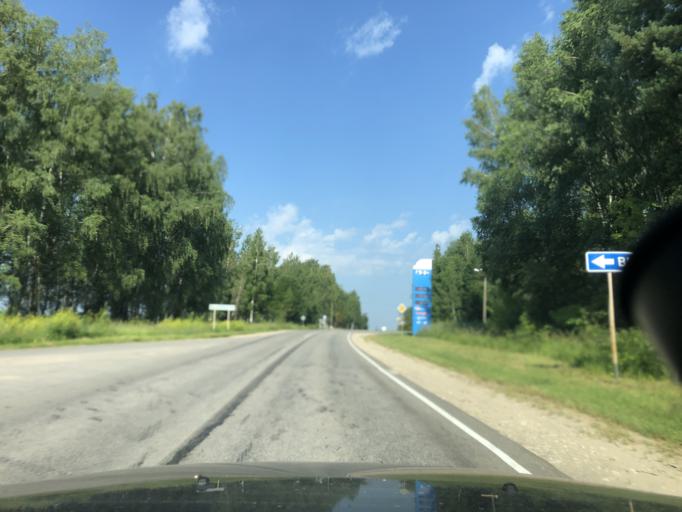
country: RU
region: Tula
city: Dubna
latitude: 54.1463
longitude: 36.9798
